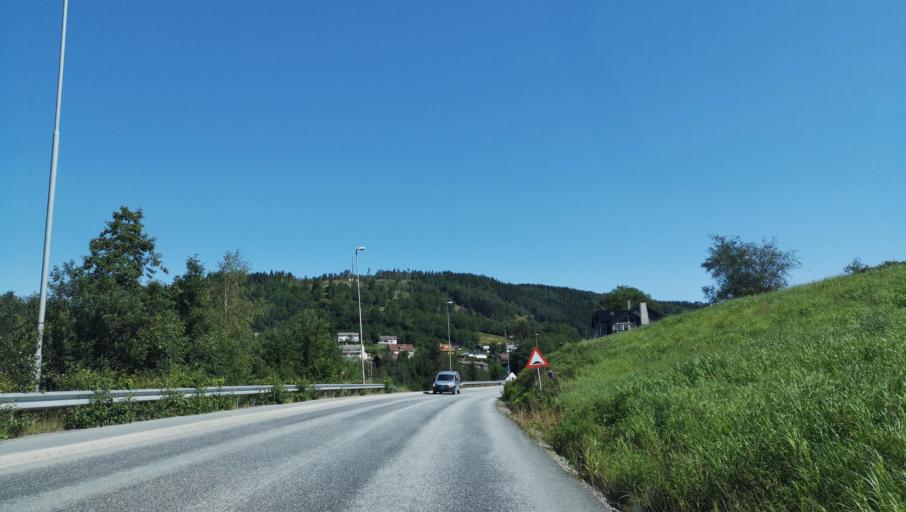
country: NO
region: Hordaland
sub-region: Voss
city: Voss
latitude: 60.6332
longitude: 6.4483
